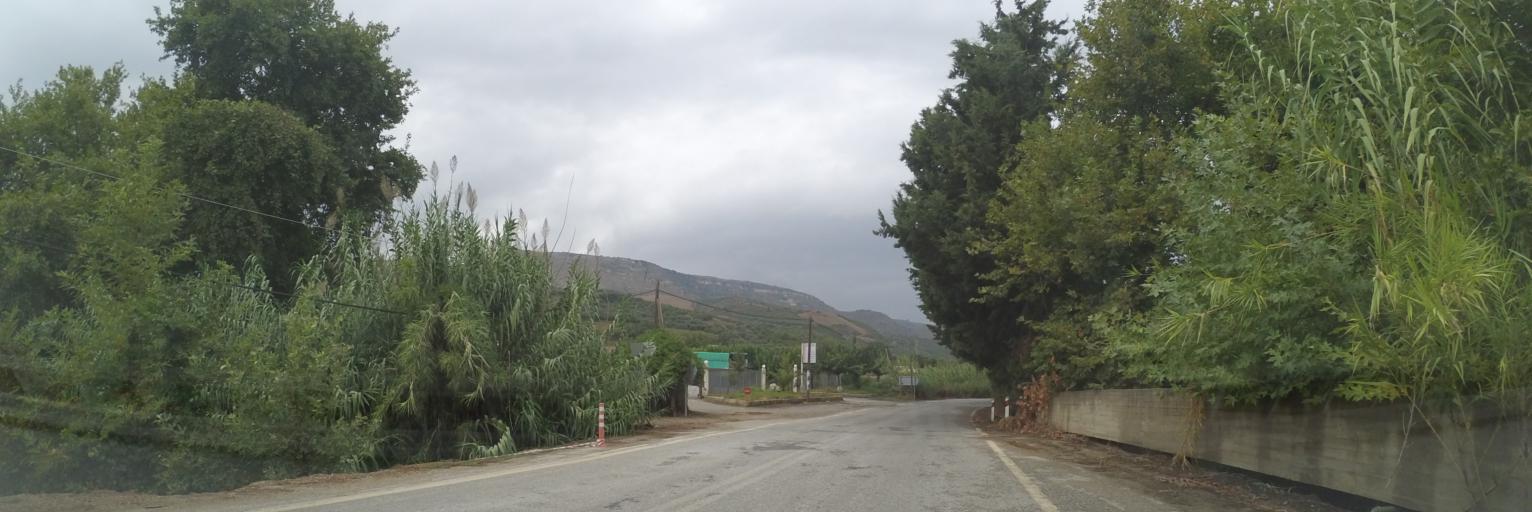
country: GR
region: Crete
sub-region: Nomos Rethymnis
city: Agia Foteini
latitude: 35.2889
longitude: 24.5624
